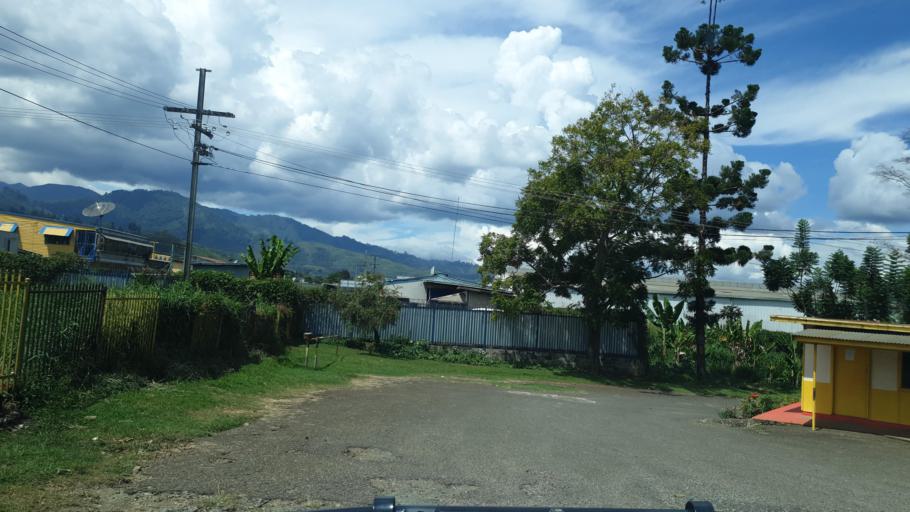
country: PG
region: Eastern Highlands
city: Goroka
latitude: -6.0845
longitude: 145.3886
